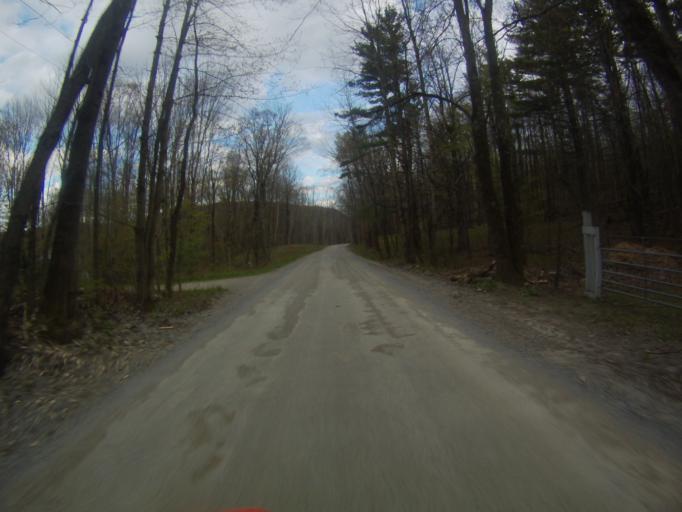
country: US
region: Vermont
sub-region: Addison County
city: Middlebury (village)
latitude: 43.9820
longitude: -73.0619
